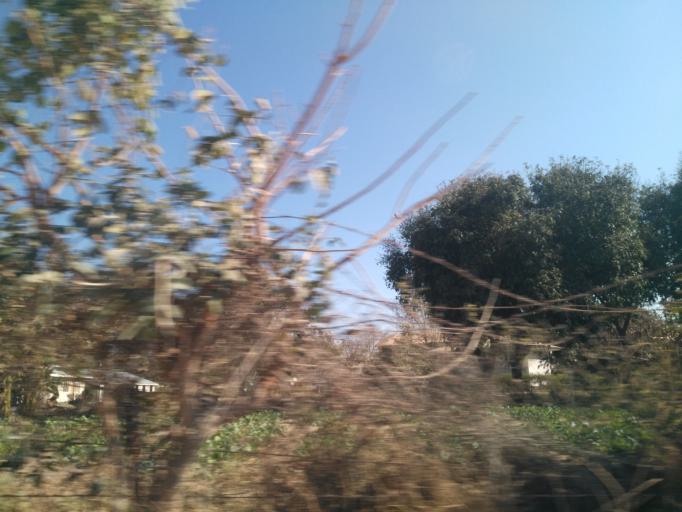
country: TZ
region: Dodoma
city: Dodoma
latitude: -6.1298
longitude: 35.7445
